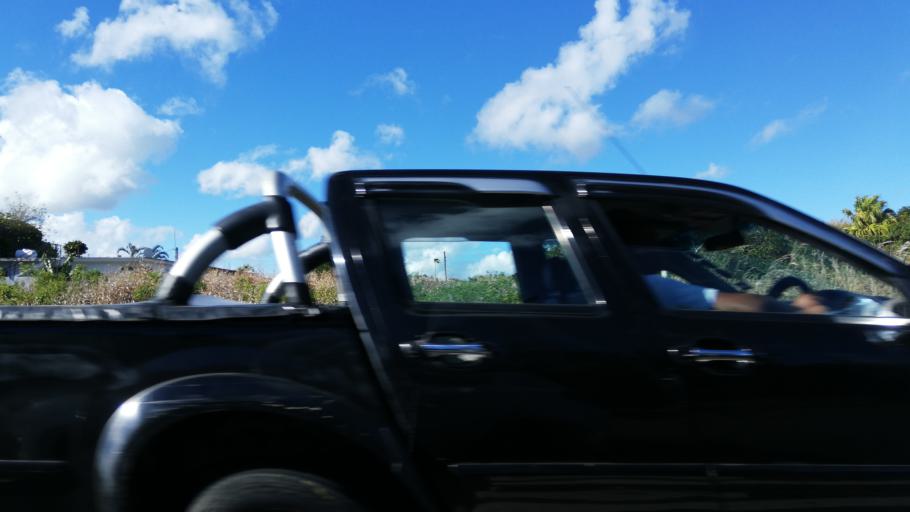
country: MU
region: Moka
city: La Dagotiere
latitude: -20.2326
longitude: 57.5567
